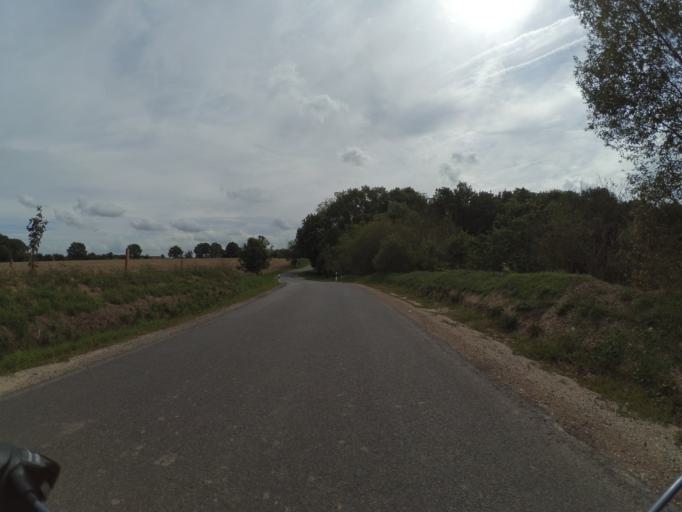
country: DE
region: Rheinland-Pfalz
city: Dodenburg
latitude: 49.9183
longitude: 6.7795
